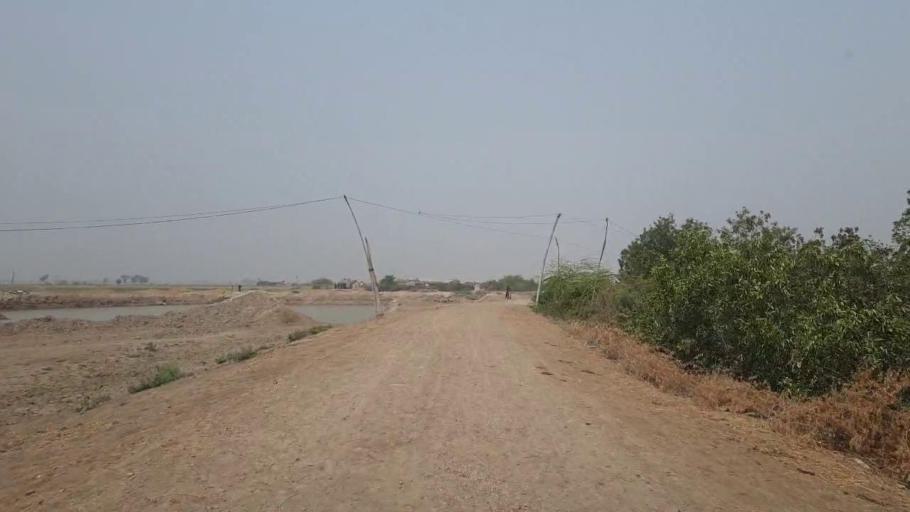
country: PK
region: Sindh
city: Kario
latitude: 24.6617
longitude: 68.6390
